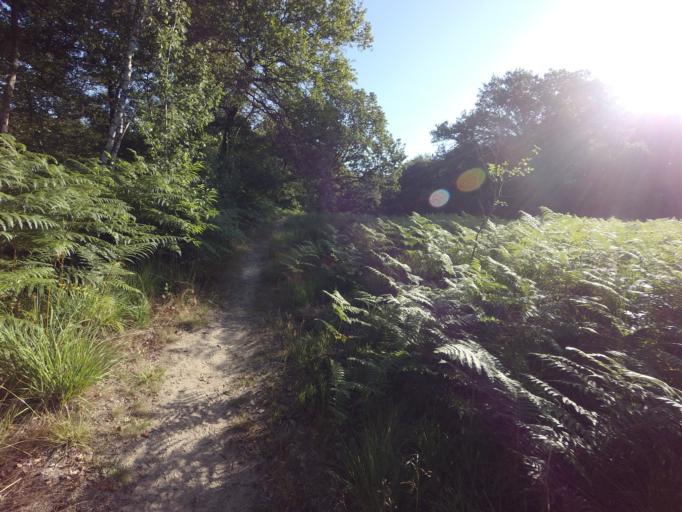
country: NL
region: Limburg
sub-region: Gemeente Roerdalen
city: Herkenbosch
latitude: 51.1753
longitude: 6.1139
